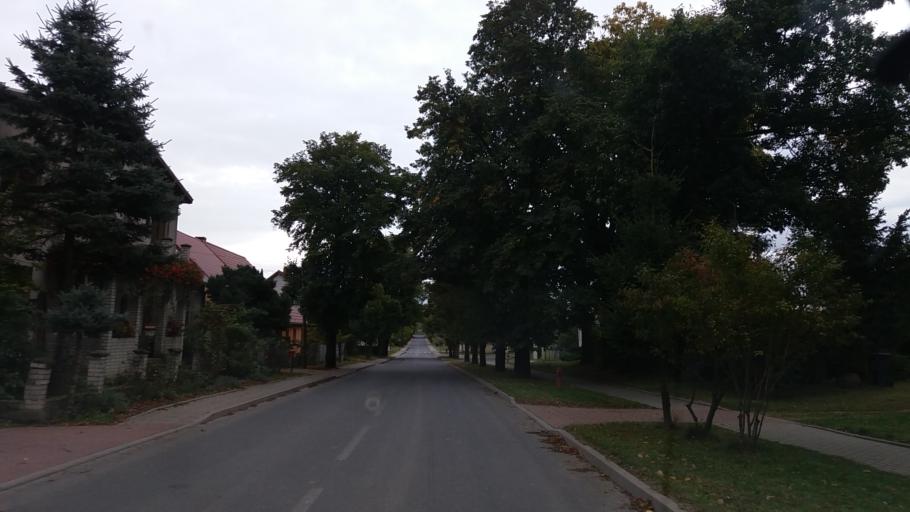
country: PL
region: West Pomeranian Voivodeship
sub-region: Powiat choszczenski
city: Pelczyce
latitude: 53.0217
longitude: 15.3680
